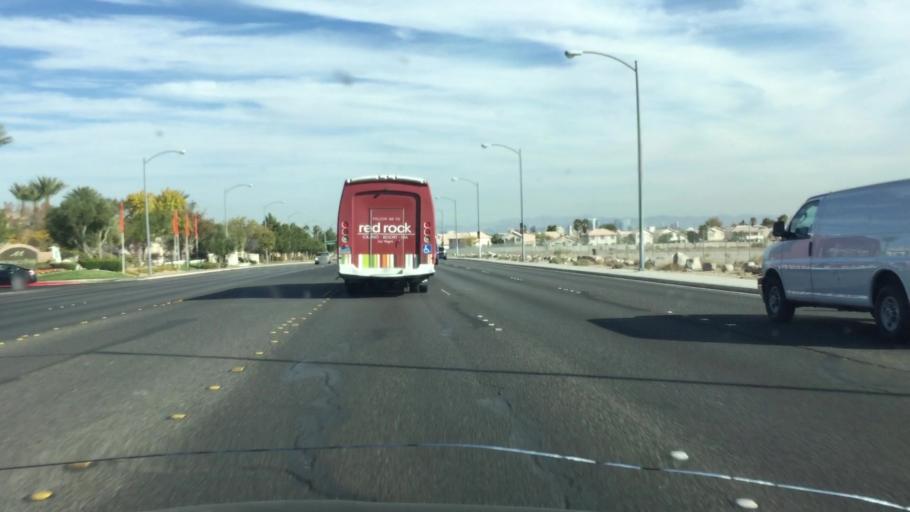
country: US
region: Nevada
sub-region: Clark County
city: Spring Valley
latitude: 36.1294
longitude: -115.2734
